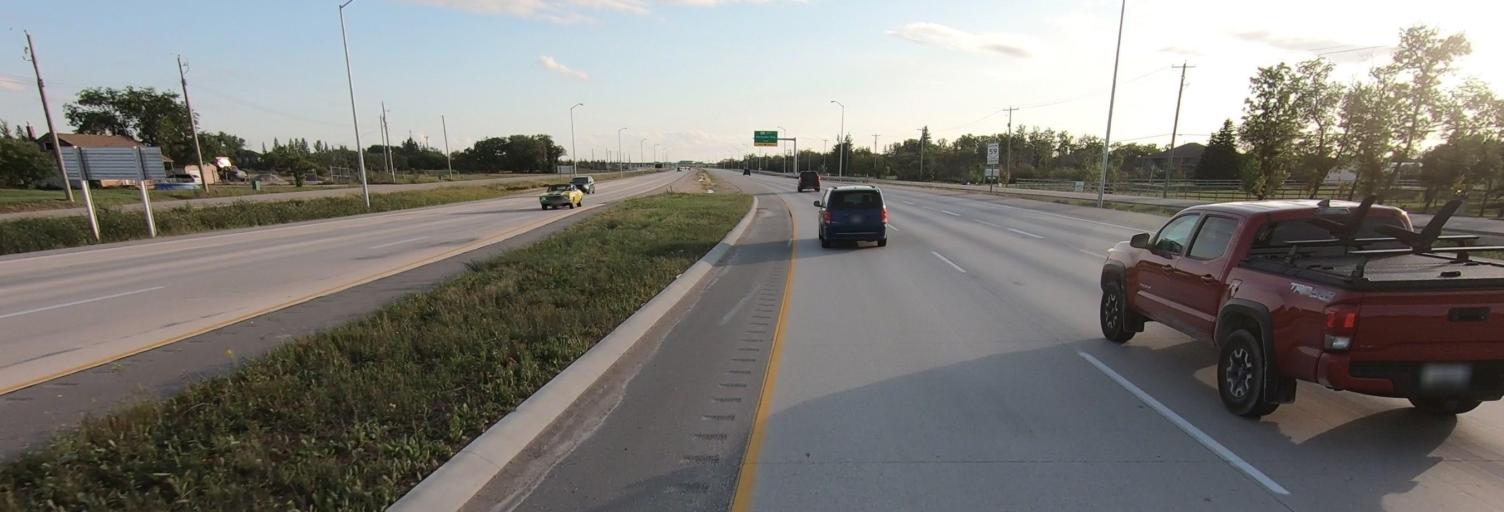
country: CA
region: Manitoba
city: Winnipeg
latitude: 49.9649
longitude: -97.0166
